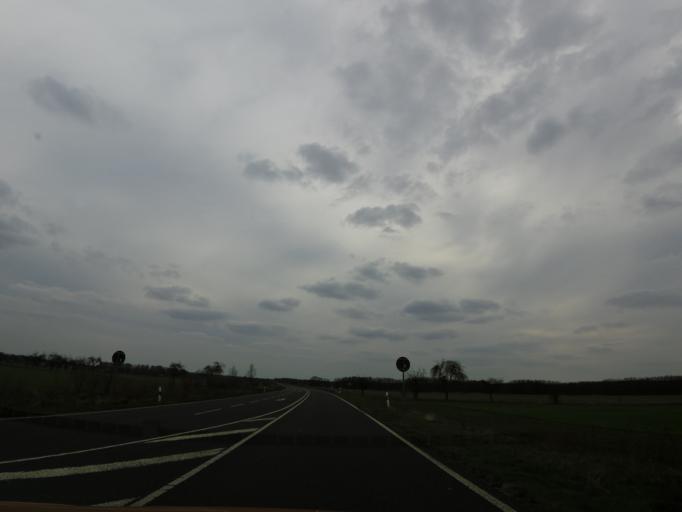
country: DE
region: Brandenburg
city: Mullrose
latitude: 52.2494
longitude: 14.3950
